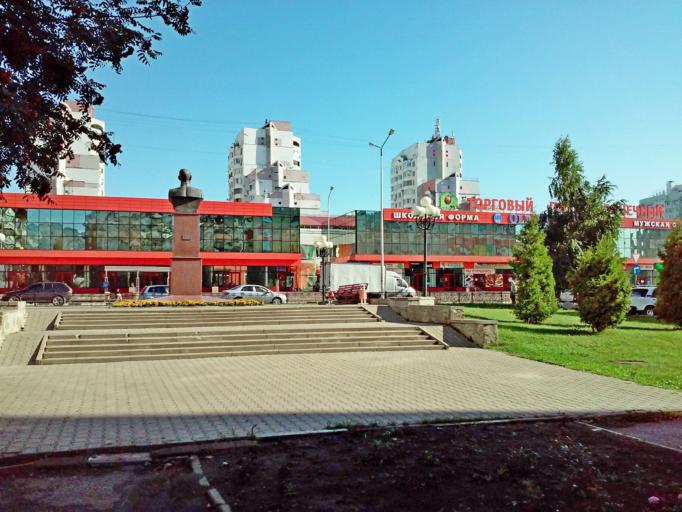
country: RU
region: Belgorod
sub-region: Belgorodskiy Rayon
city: Belgorod
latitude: 50.5598
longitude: 36.5694
